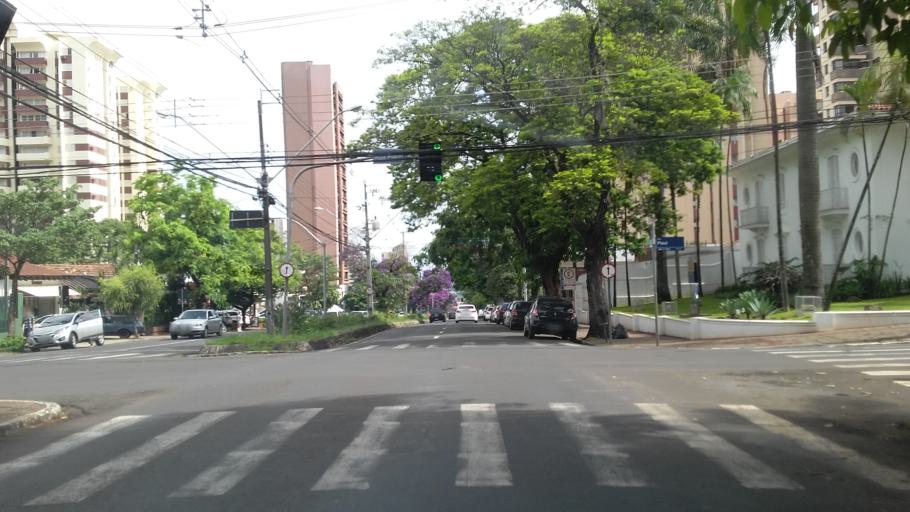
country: BR
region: Parana
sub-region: Londrina
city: Londrina
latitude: -23.3131
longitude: -51.1656
